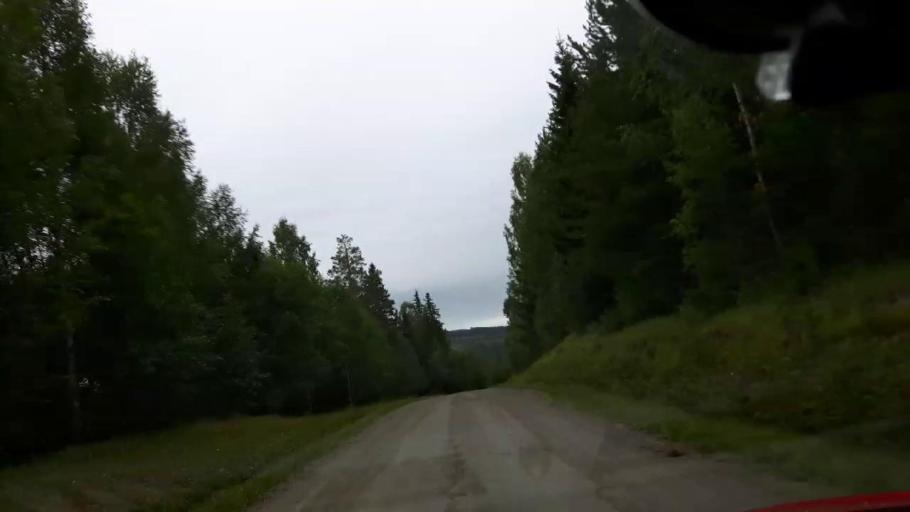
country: SE
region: Vaesternorrland
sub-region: Ange Kommun
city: Fransta
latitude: 62.8493
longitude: 15.9639
